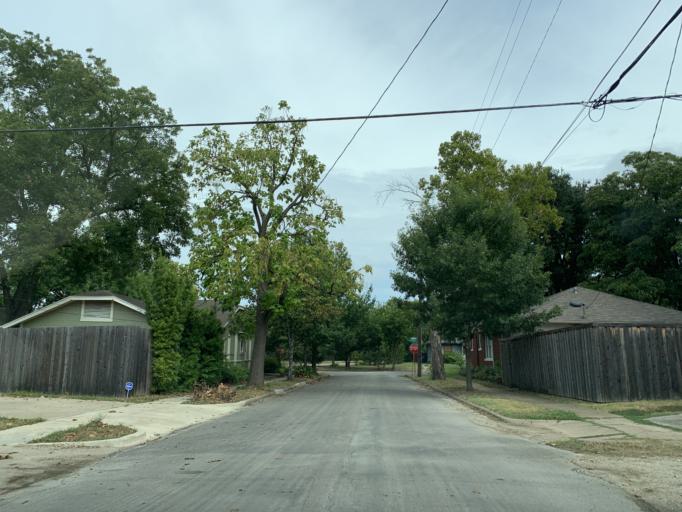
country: US
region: Texas
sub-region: Dallas County
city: Cockrell Hill
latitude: 32.7431
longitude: -96.8436
